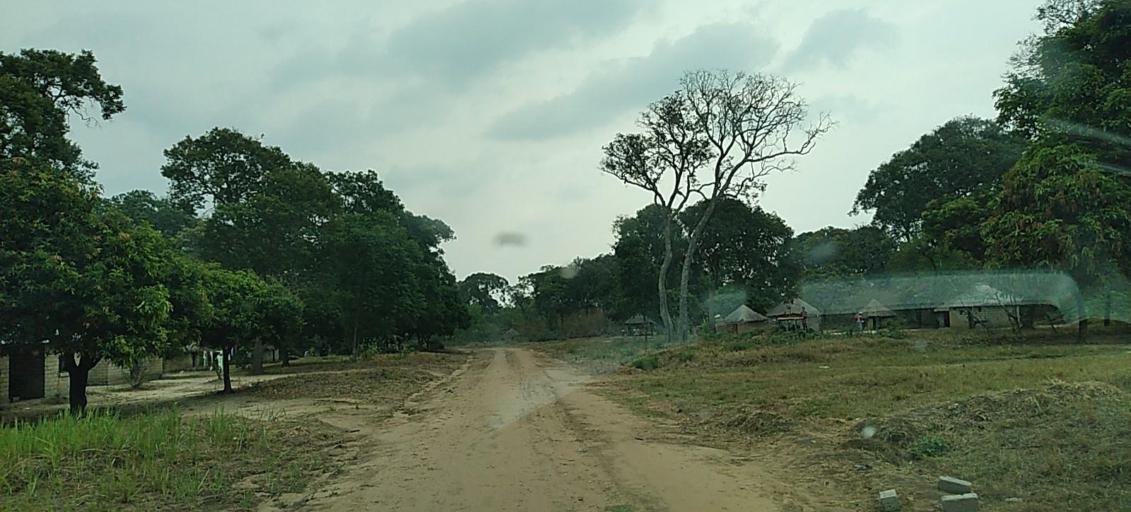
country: ZM
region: North-Western
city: Mwinilunga
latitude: -11.4208
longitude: 24.5969
